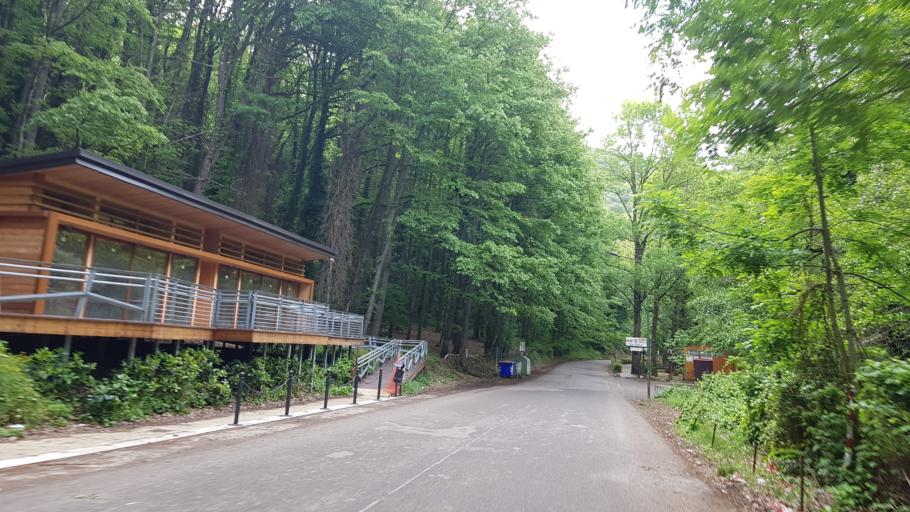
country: IT
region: Basilicate
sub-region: Provincia di Potenza
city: Rionero in Vulture
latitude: 40.9300
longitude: 15.6115
